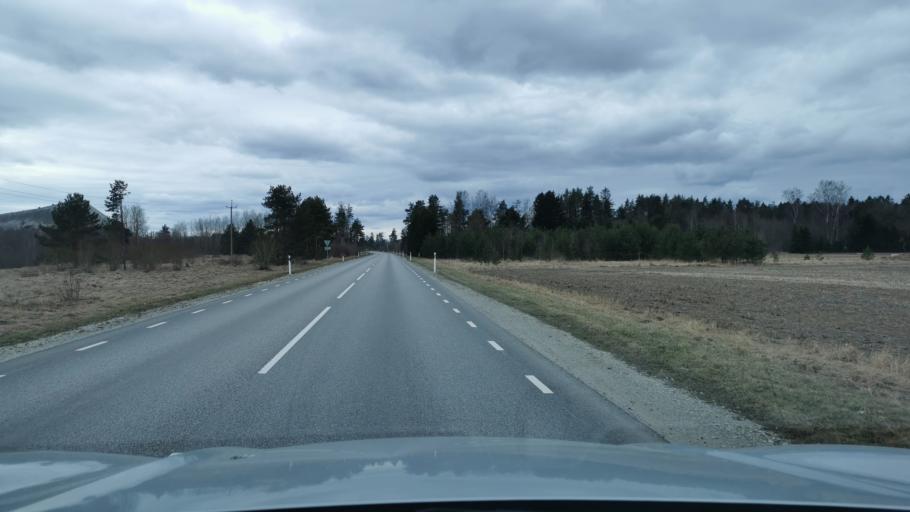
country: EE
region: Ida-Virumaa
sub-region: Puessi linn
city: Pussi
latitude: 59.3673
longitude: 27.0302
